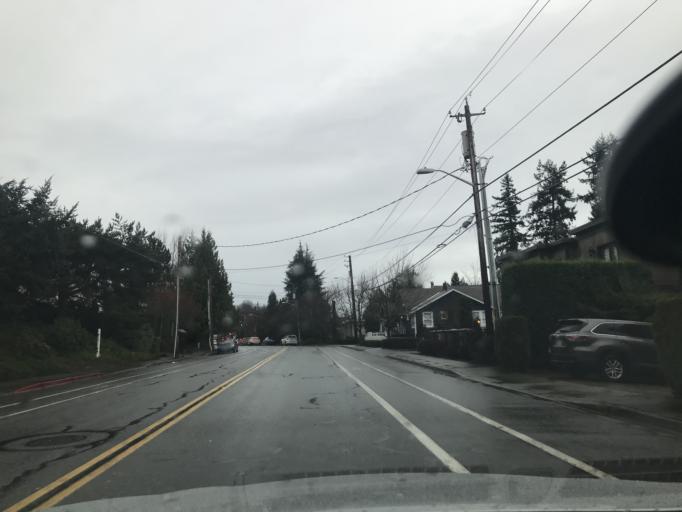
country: US
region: Washington
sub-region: King County
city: Kirkland
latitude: 47.6695
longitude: -122.2024
